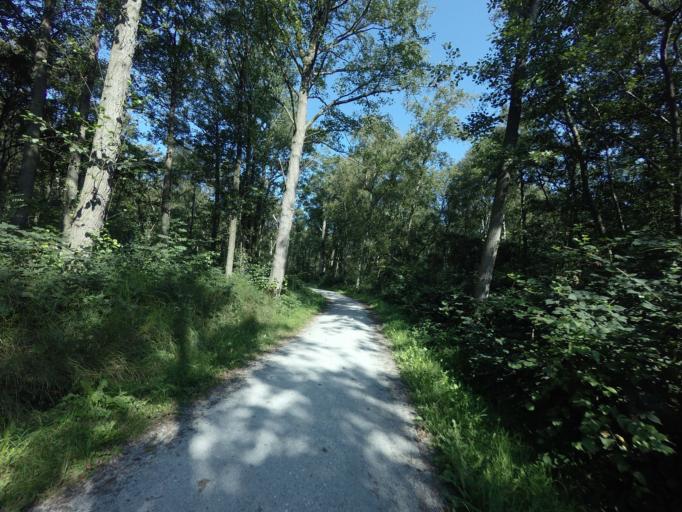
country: NL
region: Friesland
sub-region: Gemeente Schiermonnikoog
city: Schiermonnikoog
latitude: 53.4866
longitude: 6.1730
